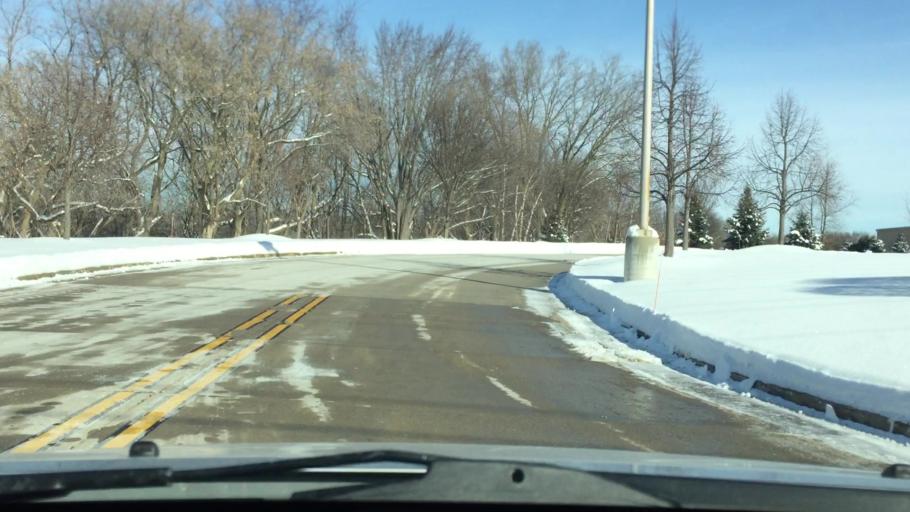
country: US
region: Wisconsin
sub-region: Waukesha County
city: Waukesha
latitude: 42.9886
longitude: -88.2613
